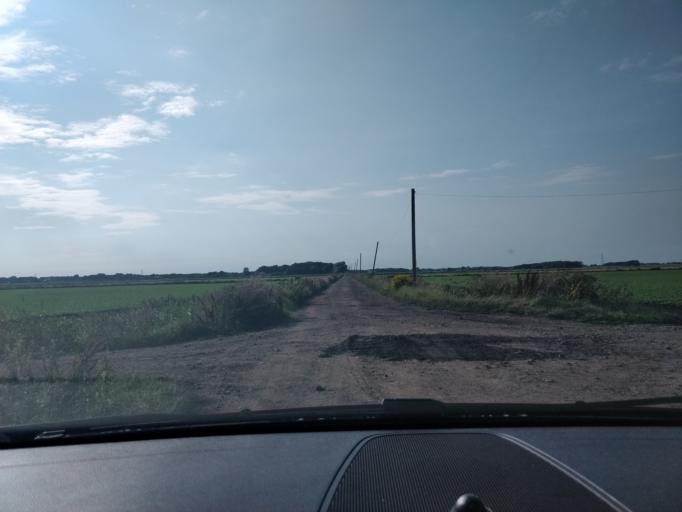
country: GB
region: England
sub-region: Lancashire
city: Banks
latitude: 53.6507
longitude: -2.9130
